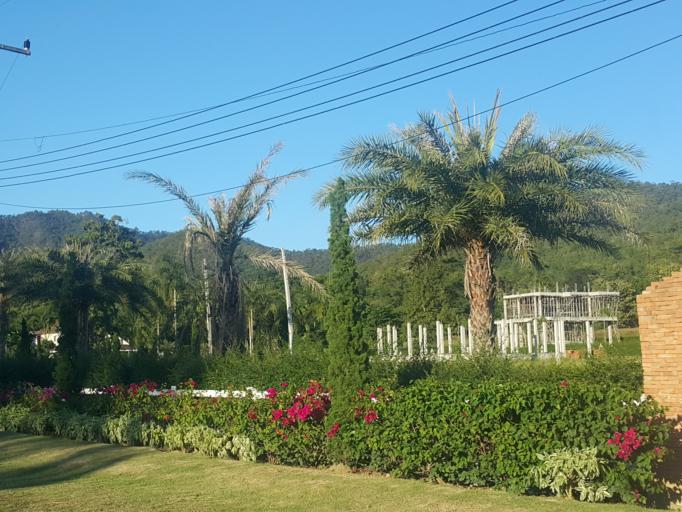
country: TH
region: Chiang Mai
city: San Sai
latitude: 18.9279
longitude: 99.1432
